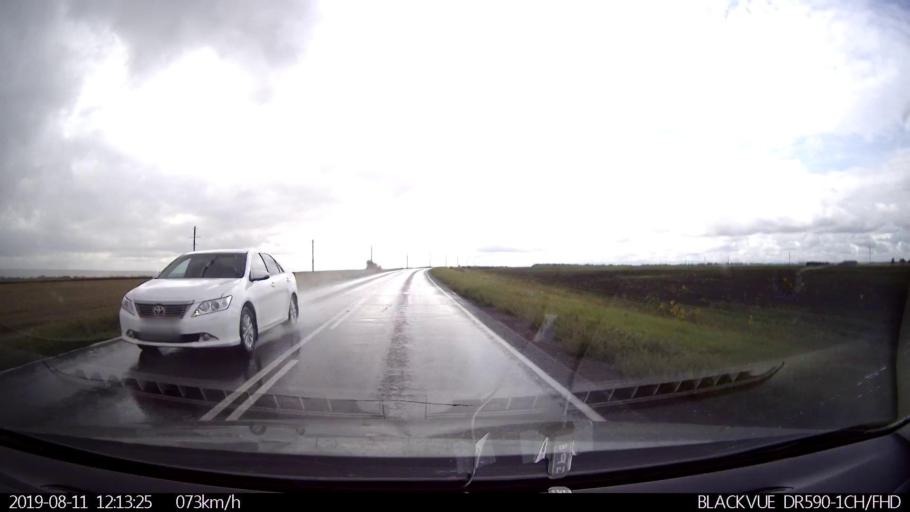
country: RU
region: Ulyanovsk
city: Silikatnyy
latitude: 53.9621
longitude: 47.9922
